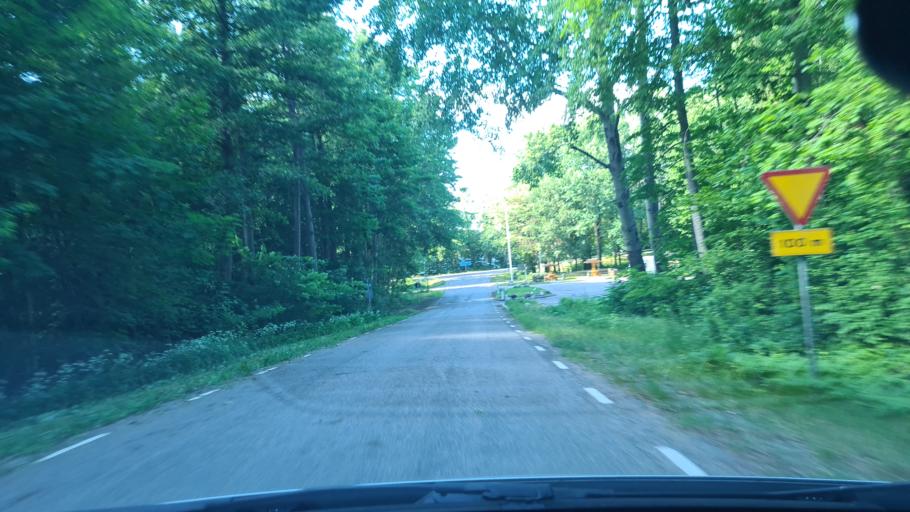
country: SE
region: OEstergoetland
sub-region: Norrkopings Kommun
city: Krokek
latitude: 58.7245
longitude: 16.4285
